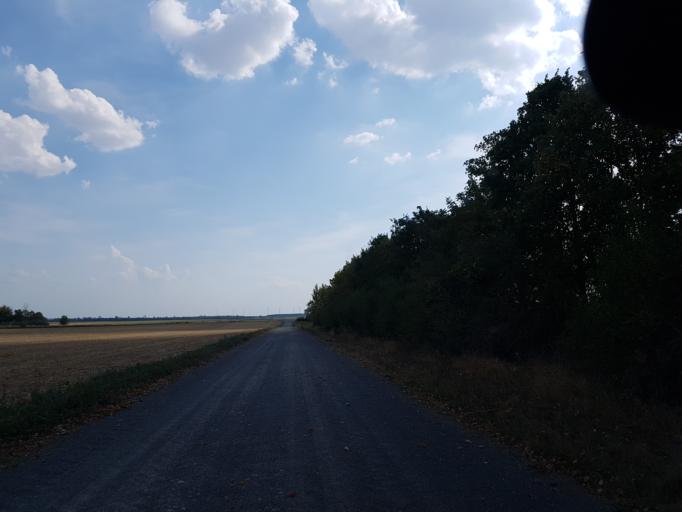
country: DE
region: Brandenburg
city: Treuenbrietzen
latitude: 51.9933
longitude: 12.8687
